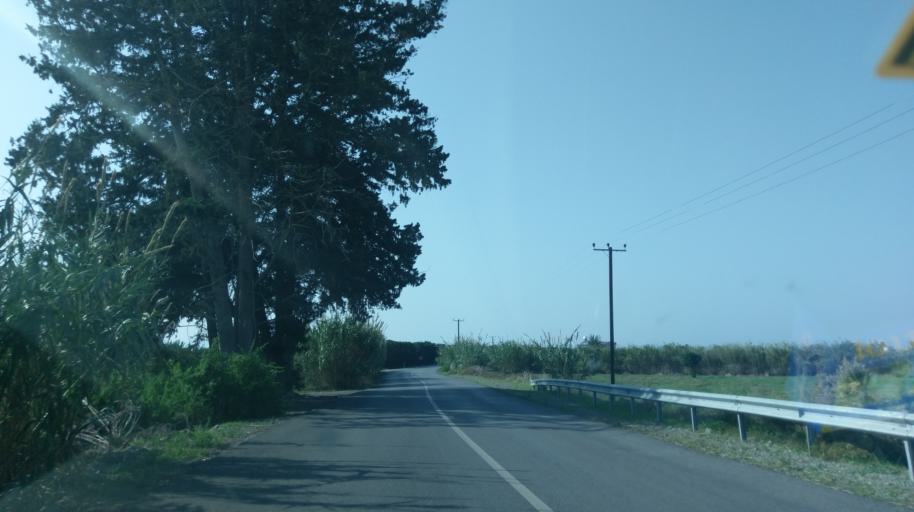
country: CY
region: Lefkosia
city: Morfou
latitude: 35.2109
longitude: 32.9666
